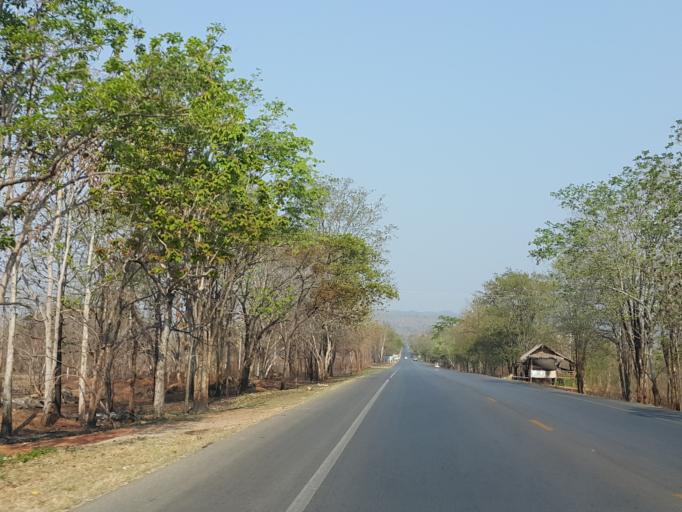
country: TH
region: Kanchanaburi
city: Sai Yok
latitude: 14.0952
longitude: 99.2572
